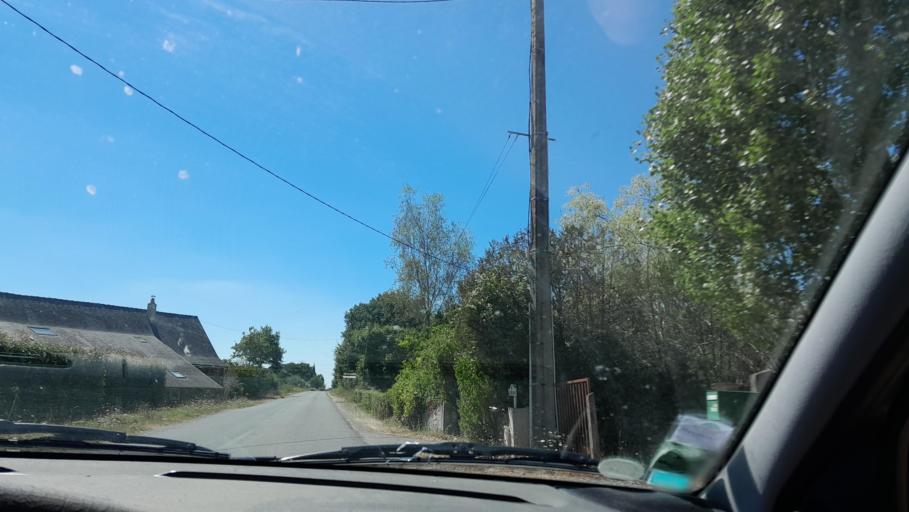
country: FR
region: Pays de la Loire
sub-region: Departement de la Mayenne
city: Congrier
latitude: 47.8314
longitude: -1.1820
